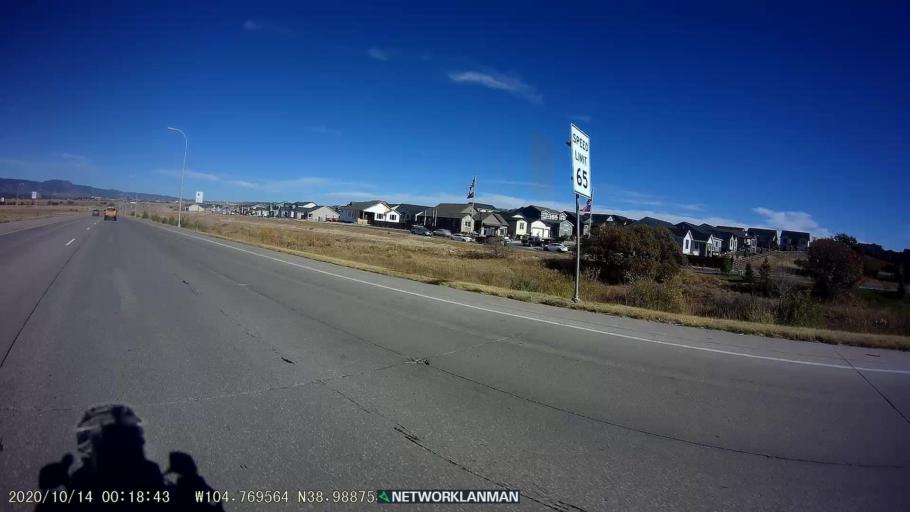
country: US
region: Colorado
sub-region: El Paso County
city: Black Forest
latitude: 38.9890
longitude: -104.7698
